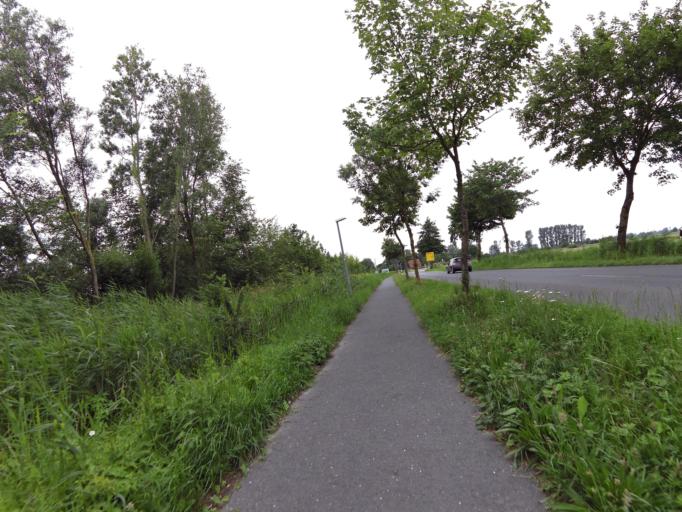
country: DE
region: Lower Saxony
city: Dorum
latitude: 53.6955
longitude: 8.5630
